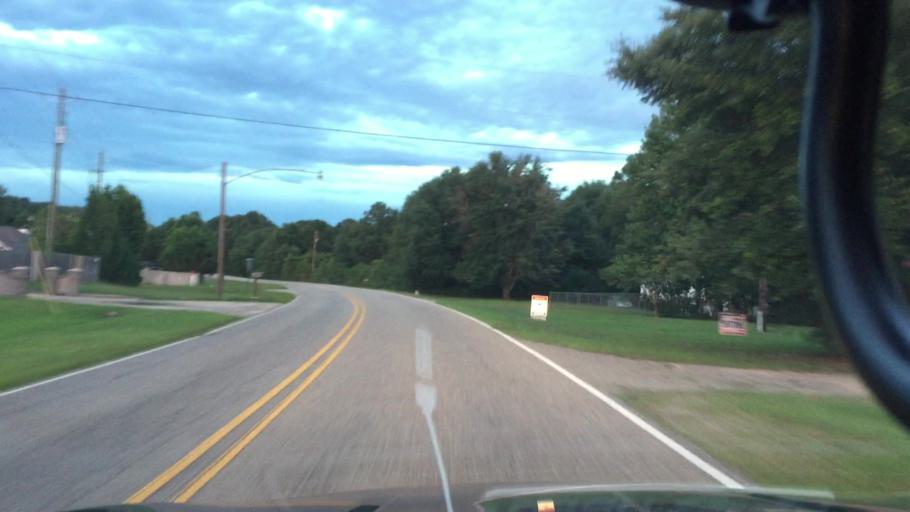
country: US
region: Alabama
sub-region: Coffee County
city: Enterprise
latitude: 31.3677
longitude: -85.8467
